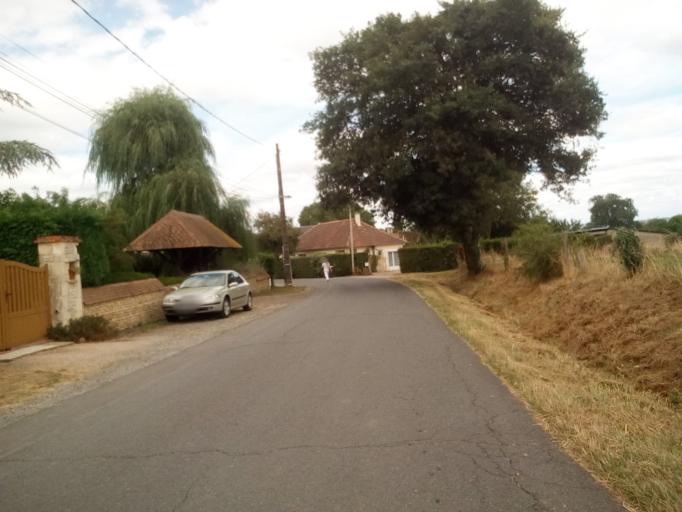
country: FR
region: Lower Normandy
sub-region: Departement du Calvados
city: Troarn
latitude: 49.1602
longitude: -0.1608
